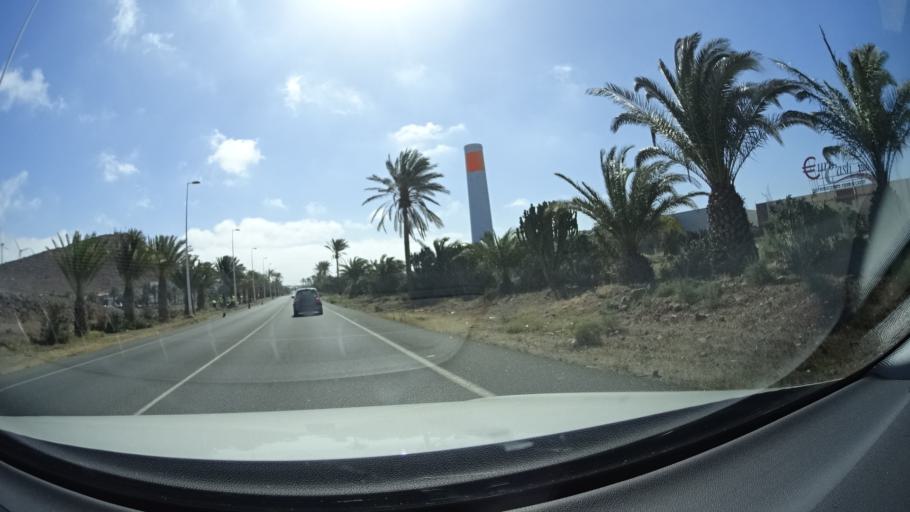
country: ES
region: Canary Islands
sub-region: Provincia de Las Palmas
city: Cruce de Arinaga
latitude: 27.8699
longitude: -15.4170
